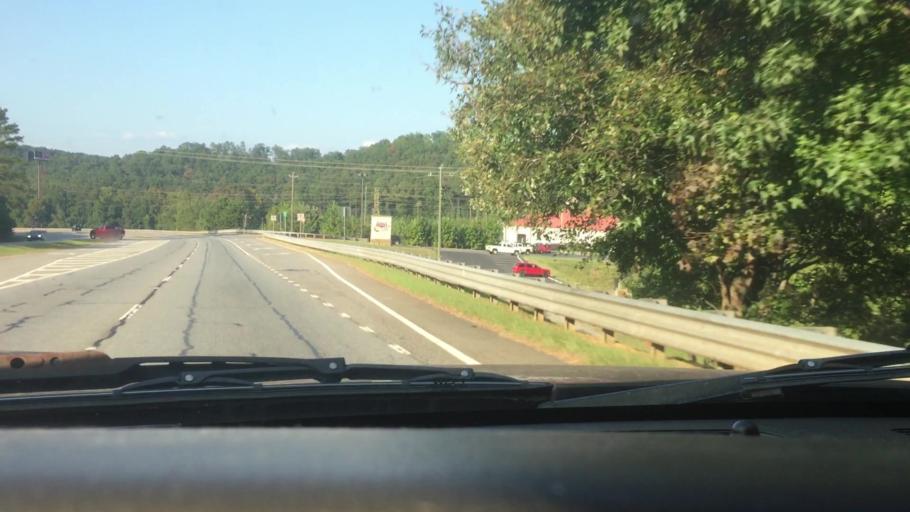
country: US
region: Georgia
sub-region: Bartow County
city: Emerson
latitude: 34.1442
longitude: -84.7473
